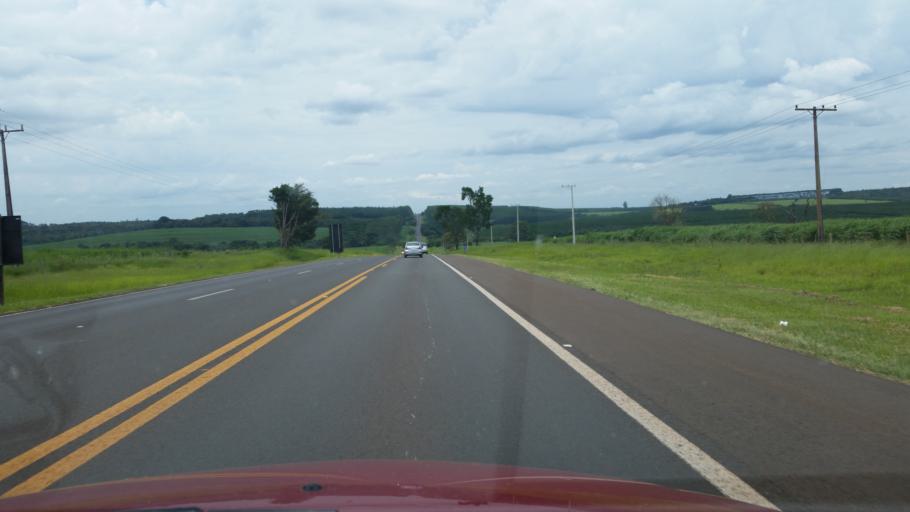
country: BR
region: Sao Paulo
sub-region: Avare
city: Avare
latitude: -23.0067
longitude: -48.8475
